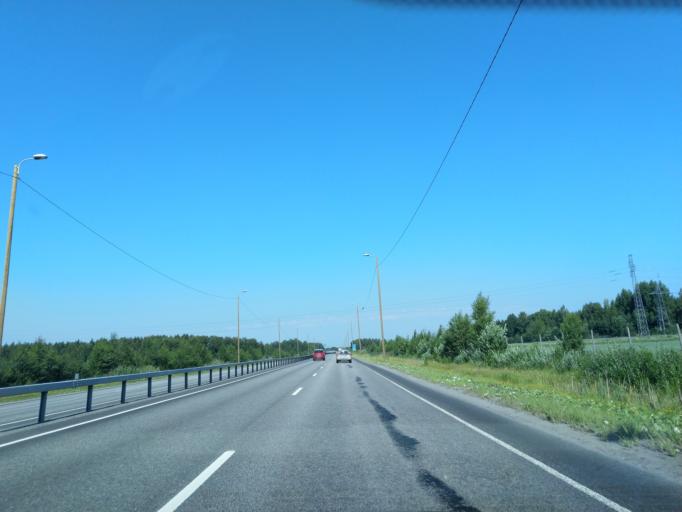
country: FI
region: Satakunta
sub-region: Pori
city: Nakkila
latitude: 61.3396
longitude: 22.0394
